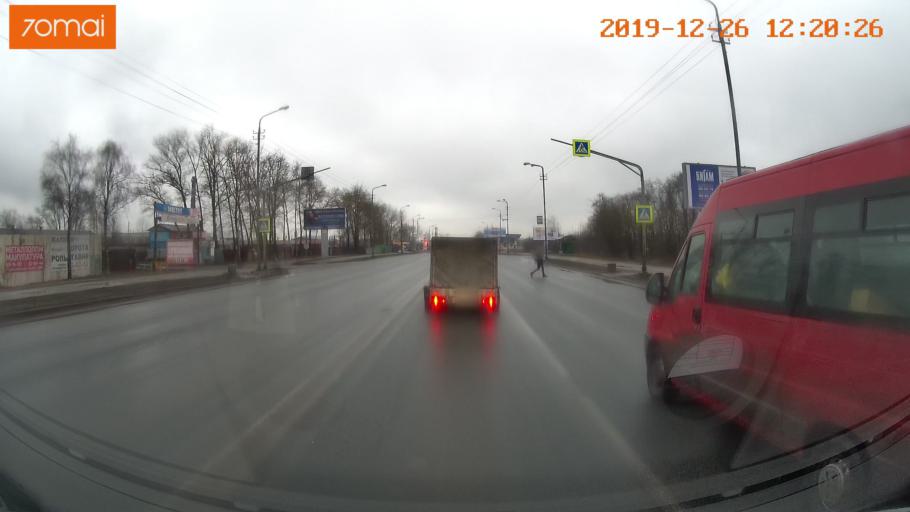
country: RU
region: Vologda
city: Tonshalovo
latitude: 59.1585
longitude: 37.9325
